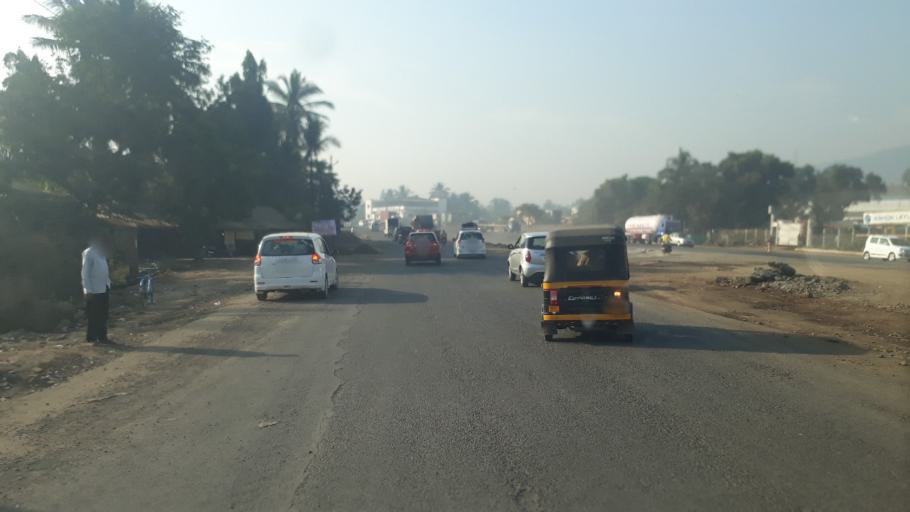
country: IN
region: Maharashtra
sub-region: Raigarh
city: Kalundri
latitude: 18.9592
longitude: 73.1311
